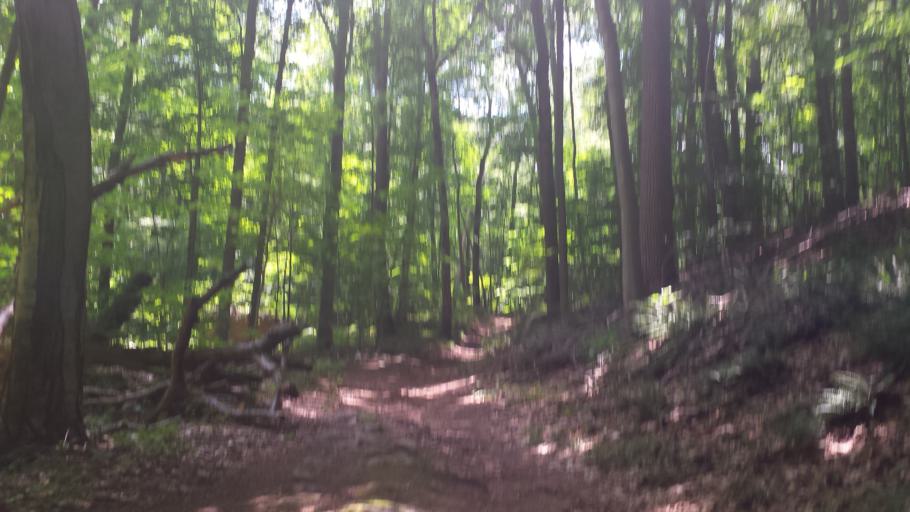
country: US
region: New York
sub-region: Westchester County
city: Scarsdale
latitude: 40.9890
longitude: -73.7555
